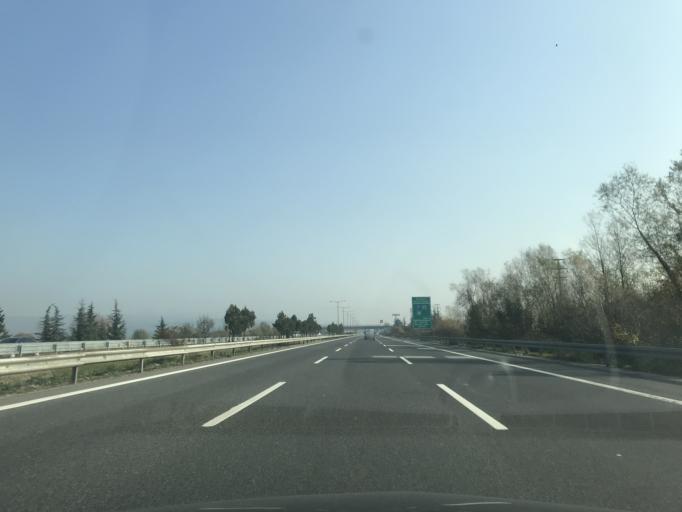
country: TR
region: Duzce
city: Duzce
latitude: 40.7906
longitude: 31.2289
